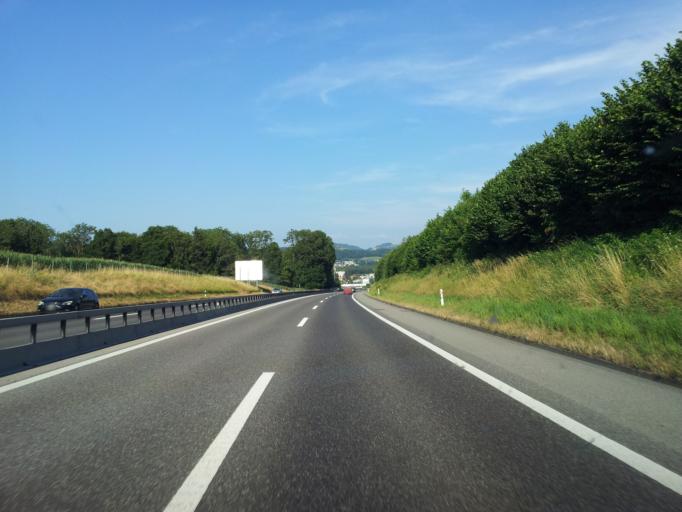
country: CH
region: Fribourg
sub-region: Sense District
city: Flamatt
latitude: 46.8888
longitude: 7.3028
